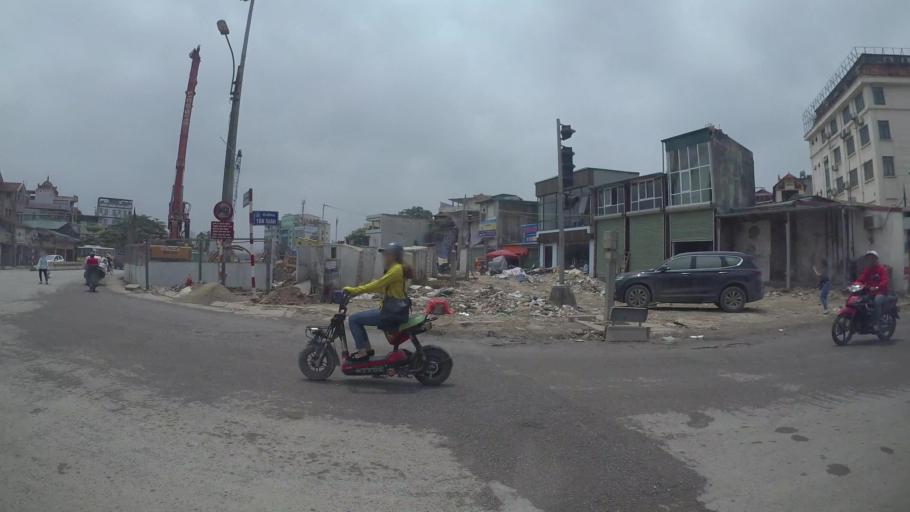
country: VN
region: Ha Noi
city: Tay Ho
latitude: 21.0780
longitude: 105.7869
